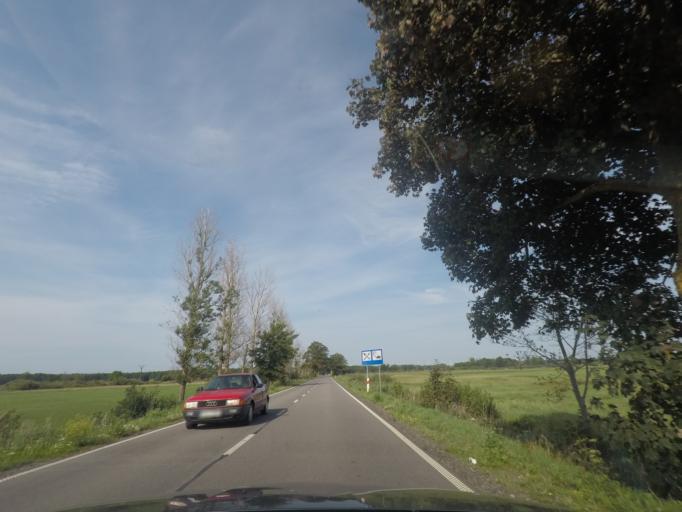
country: PL
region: Pomeranian Voivodeship
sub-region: Powiat leborski
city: Leba
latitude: 54.6515
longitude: 17.5583
